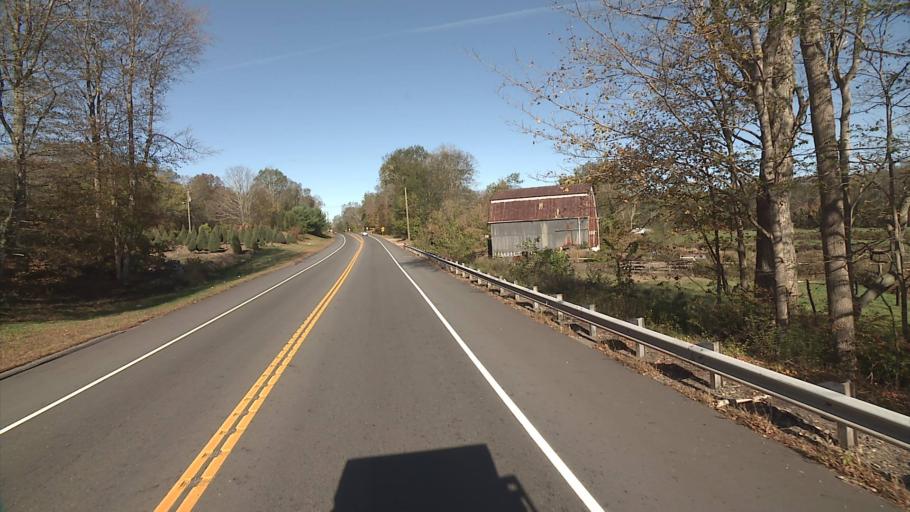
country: US
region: Connecticut
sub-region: Tolland County
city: Coventry Lake
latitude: 41.7352
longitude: -72.3605
